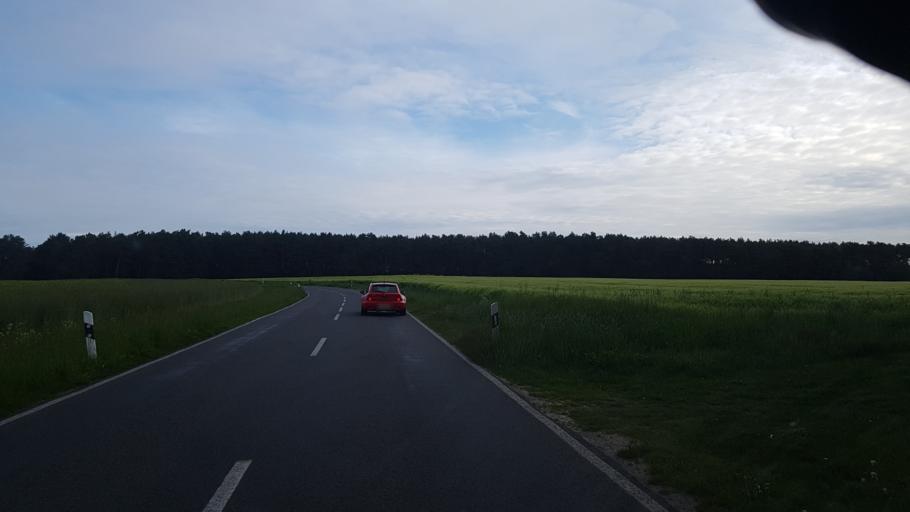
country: DE
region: Brandenburg
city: Baruth
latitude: 51.9896
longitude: 13.4822
